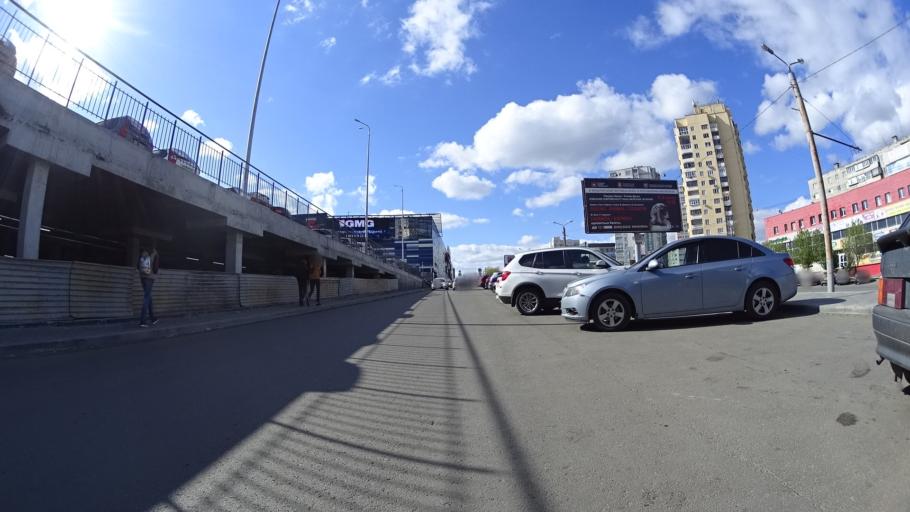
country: RU
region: Chelyabinsk
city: Roshchino
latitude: 55.1798
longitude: 61.2953
